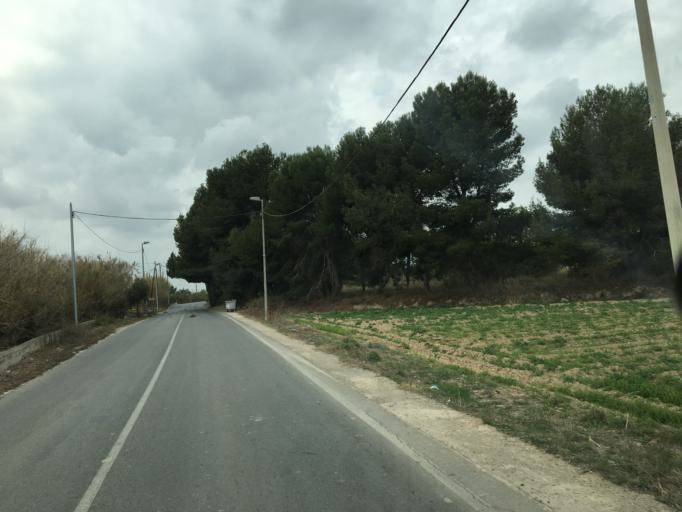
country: ES
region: Murcia
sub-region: Murcia
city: Beniel
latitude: 38.0314
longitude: -1.0190
